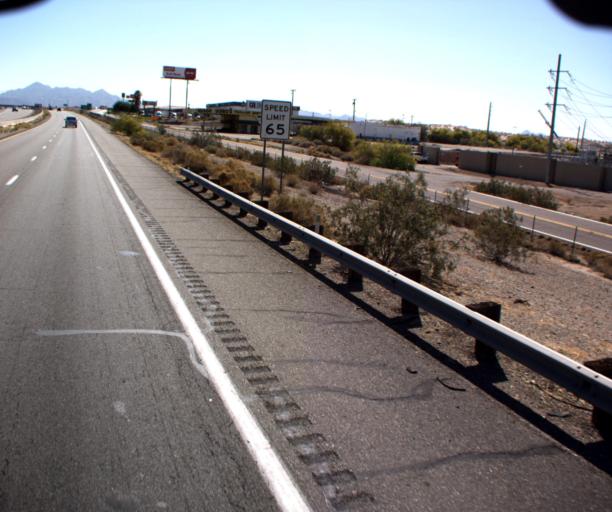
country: US
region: Arizona
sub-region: La Paz County
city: Ehrenberg
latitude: 33.6038
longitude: -114.5276
